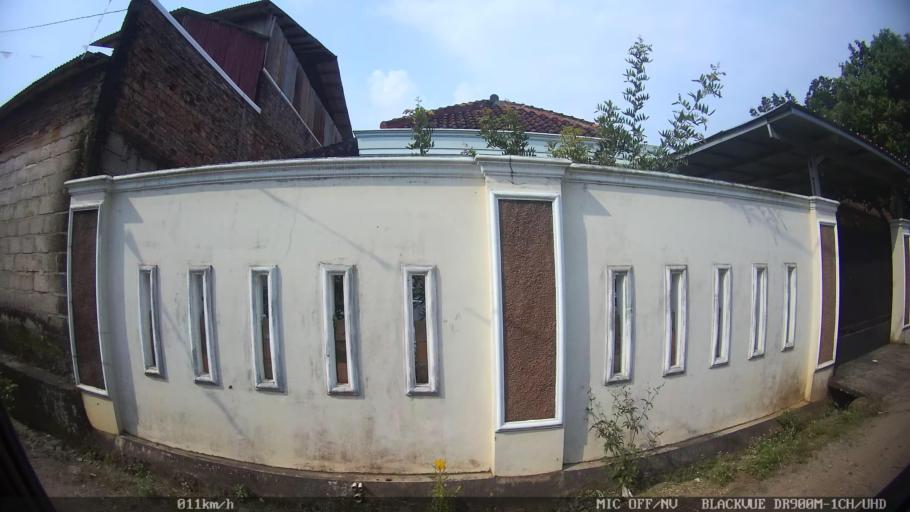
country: ID
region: Lampung
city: Kedaton
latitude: -5.3623
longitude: 105.2172
